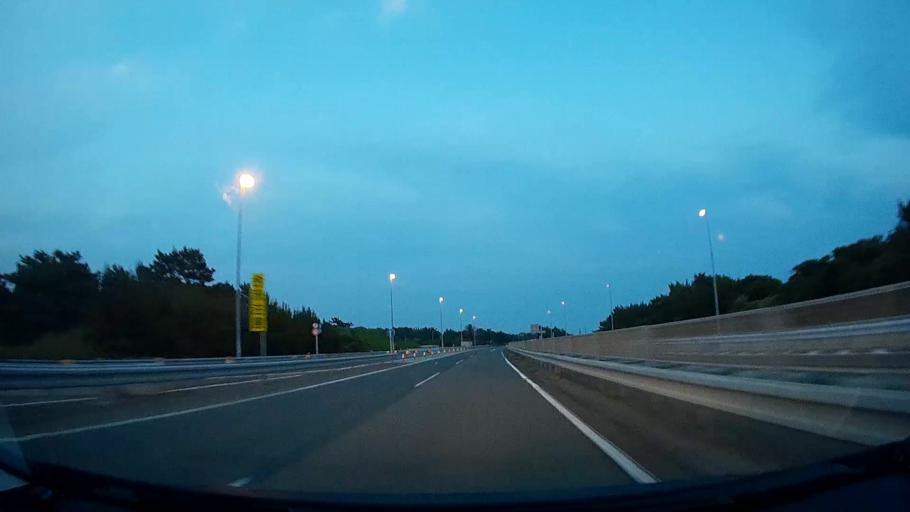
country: JP
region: Shizuoka
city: Kosai-shi
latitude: 34.6810
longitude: 137.5818
